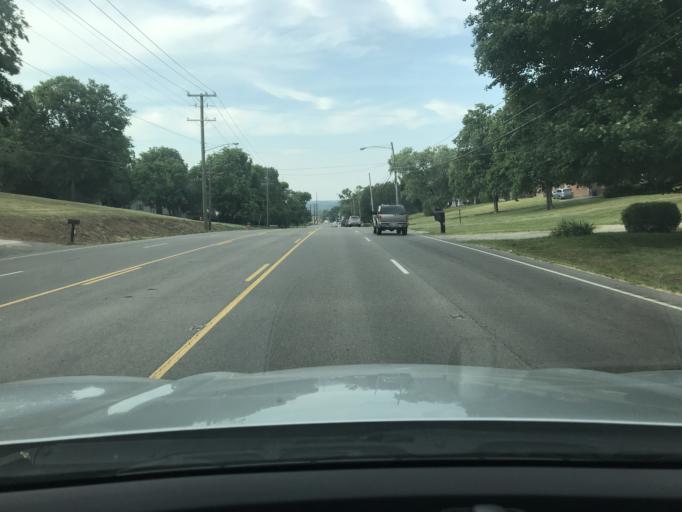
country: US
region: Tennessee
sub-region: Davidson County
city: Goodlettsville
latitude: 36.3096
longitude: -86.7164
